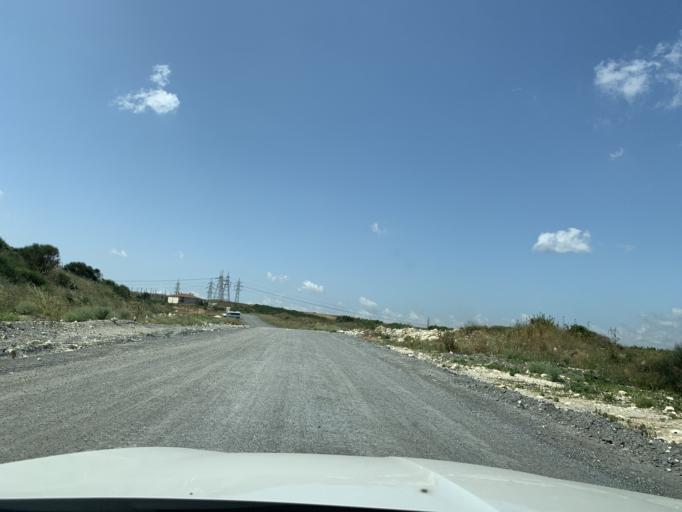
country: TR
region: Istanbul
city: Esenyurt
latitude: 41.0846
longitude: 28.6935
